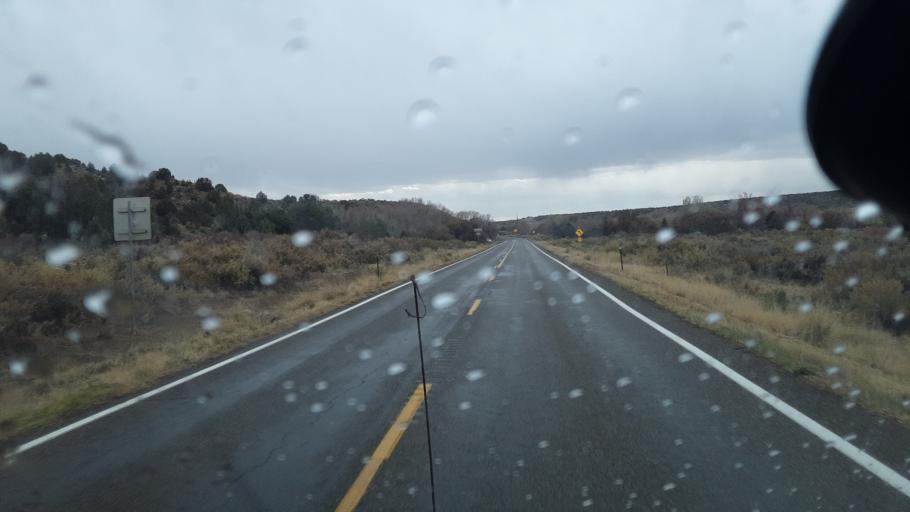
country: US
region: New Mexico
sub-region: San Juan County
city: Spencerville
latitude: 37.0027
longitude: -108.1849
